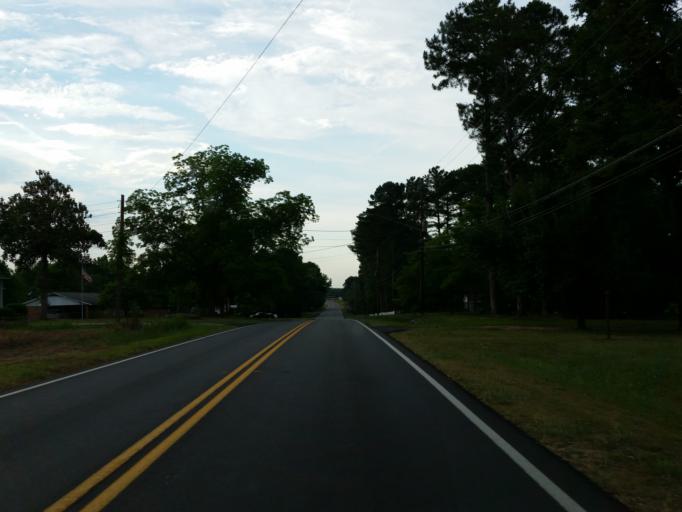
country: US
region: Georgia
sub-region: Dooly County
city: Unadilla
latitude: 32.2700
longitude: -83.7371
